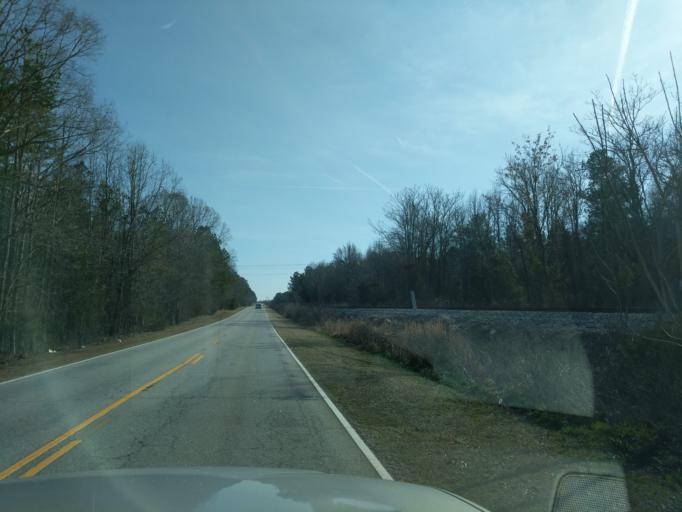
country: US
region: South Carolina
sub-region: Spartanburg County
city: Woodruff
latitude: 34.7128
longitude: -82.0195
